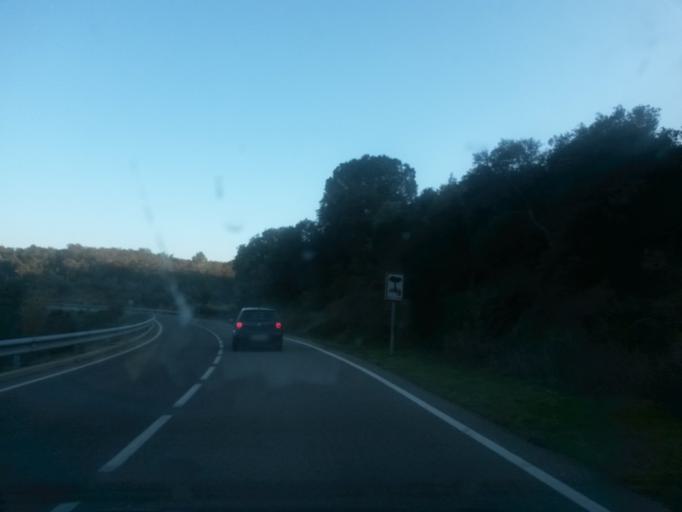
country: ES
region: Catalonia
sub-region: Provincia de Girona
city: Darnius
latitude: 42.3666
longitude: 2.8262
